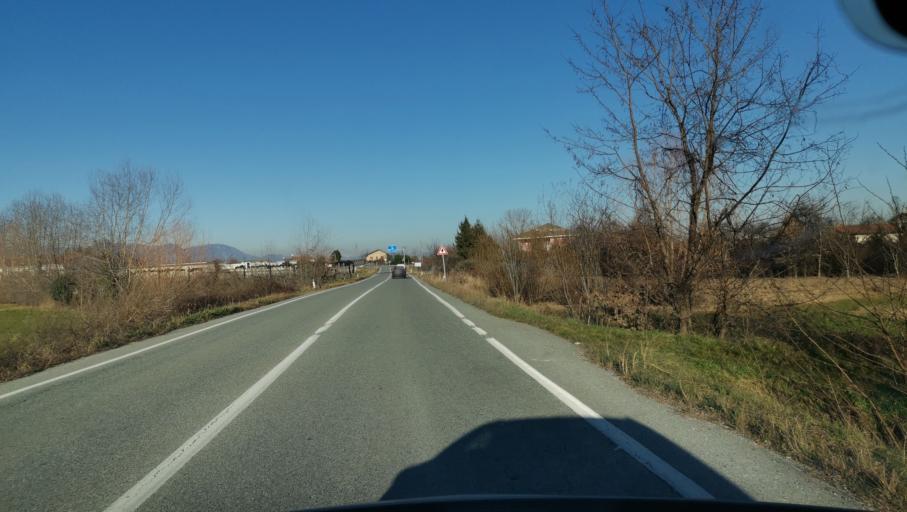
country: IT
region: Piedmont
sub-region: Provincia di Torino
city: Bibiana
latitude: 44.7927
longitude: 7.2947
